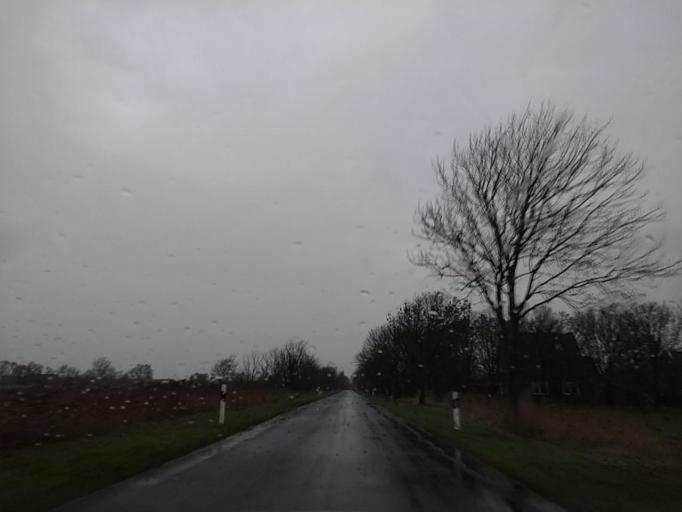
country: DE
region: Lower Saxony
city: Emden
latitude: 53.3128
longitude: 7.2538
